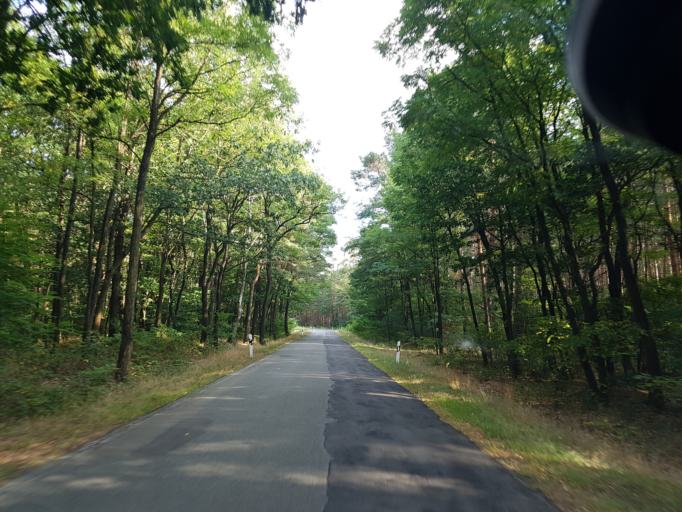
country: DE
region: Brandenburg
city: Bronkow
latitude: 51.6876
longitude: 13.8885
